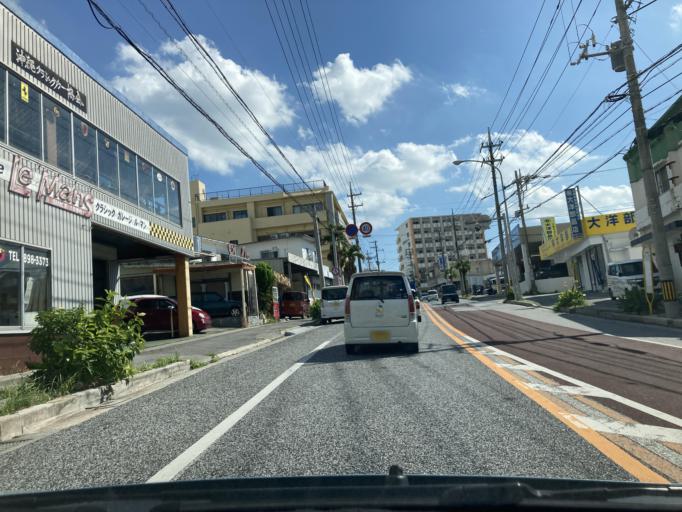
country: JP
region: Okinawa
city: Ginowan
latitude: 26.2646
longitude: 127.7392
